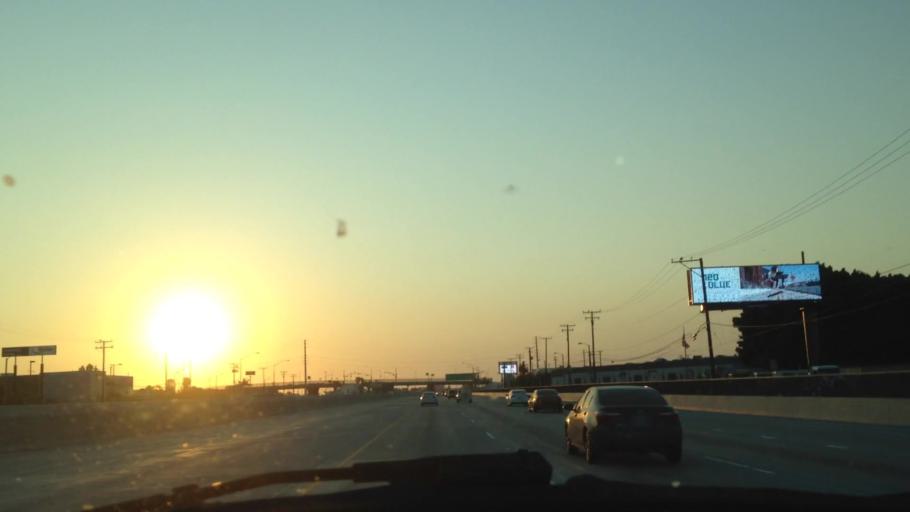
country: US
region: California
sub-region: Los Angeles County
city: La Mirada
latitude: 33.8904
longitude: -118.0400
